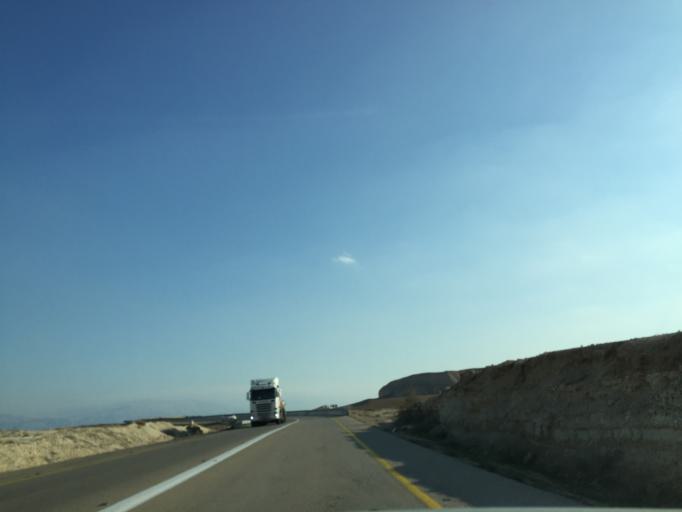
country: IL
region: Southern District
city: `En Boqeq
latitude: 31.1690
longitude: 35.3166
